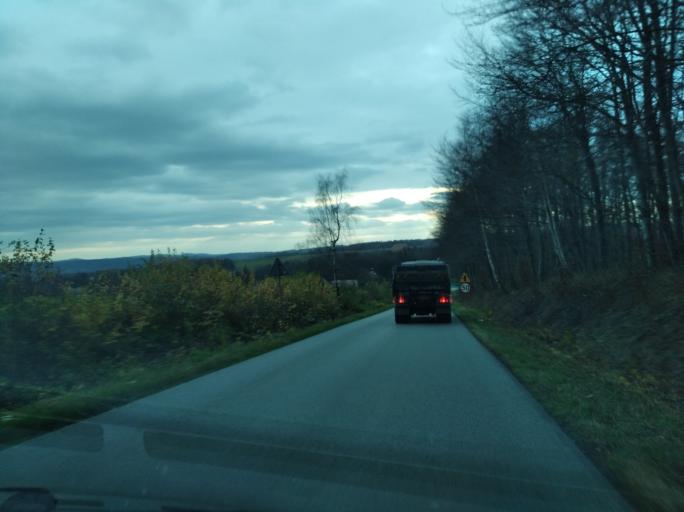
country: PL
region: Subcarpathian Voivodeship
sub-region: Powiat ropczycko-sedziszowski
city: Wielopole Skrzynskie
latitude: 49.9409
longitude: 21.6924
